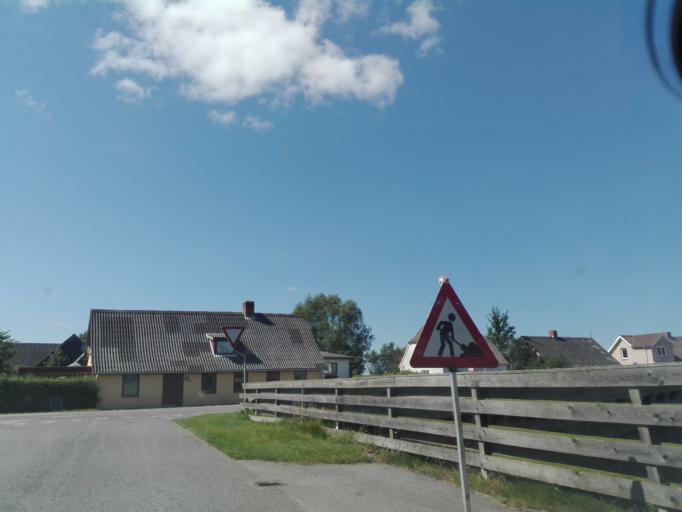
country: DK
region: Central Jutland
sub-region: Norddjurs Kommune
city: Allingabro
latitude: 56.6119
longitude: 10.2977
